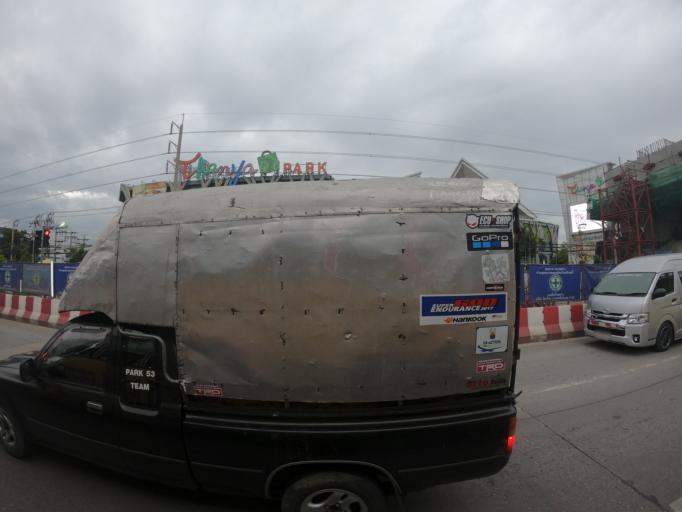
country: TH
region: Bangkok
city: Suan Luang
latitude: 13.7259
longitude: 100.6416
